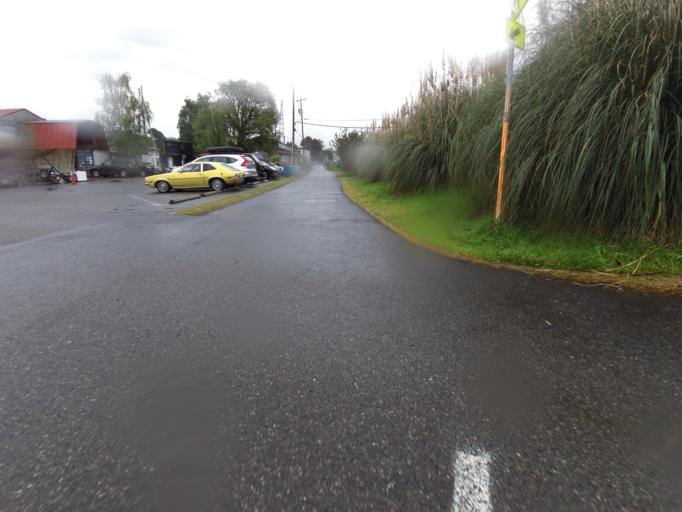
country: US
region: Washington
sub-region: King County
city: Seattle
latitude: 47.6528
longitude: -122.3657
